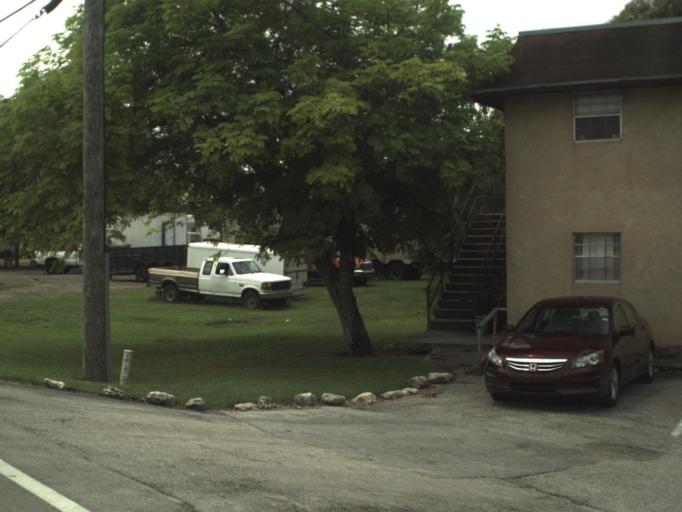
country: US
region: Florida
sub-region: Palm Beach County
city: Belle Glade
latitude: 26.6841
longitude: -80.6639
